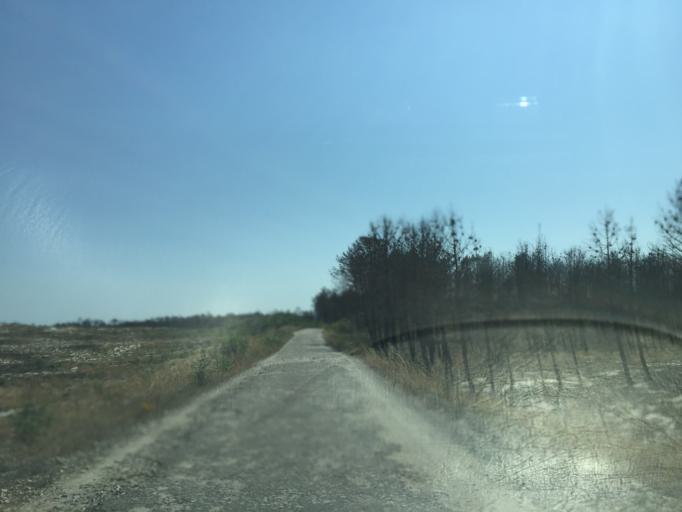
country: PT
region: Coimbra
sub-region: Figueira da Foz
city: Alhadas
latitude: 40.2593
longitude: -8.8351
